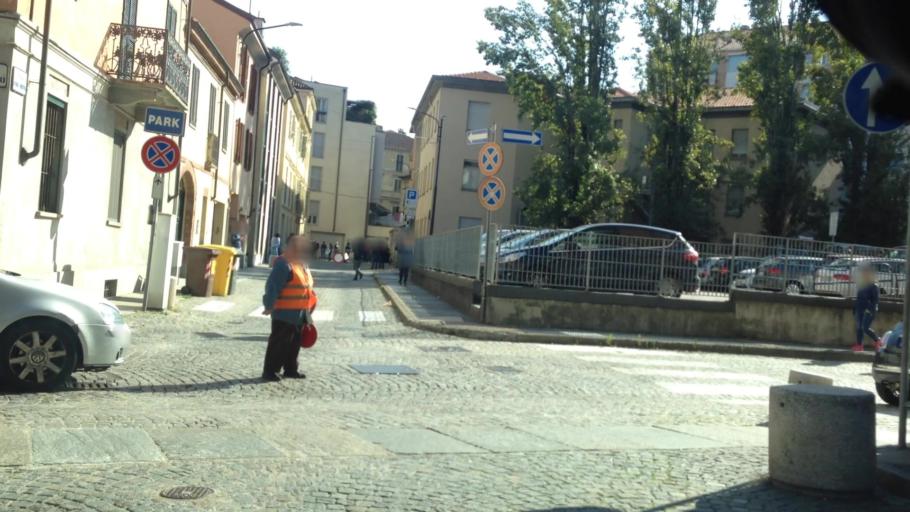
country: IT
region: Piedmont
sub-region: Provincia di Asti
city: Asti
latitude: 44.8966
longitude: 8.2058
